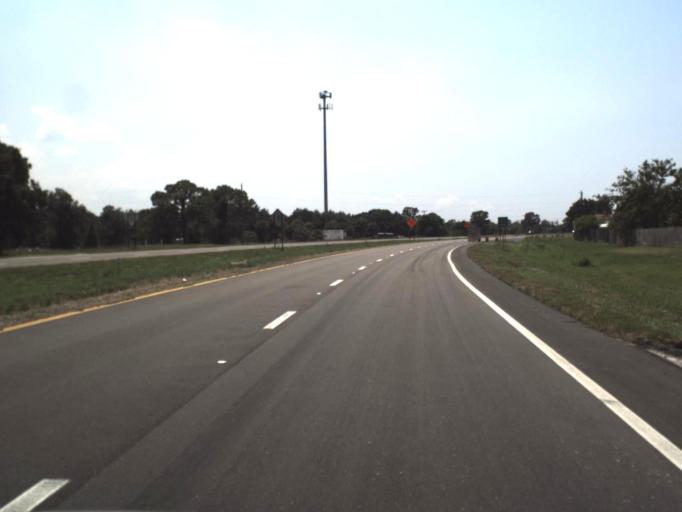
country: US
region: Florida
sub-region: Hillsborough County
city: Ruskin
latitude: 27.6764
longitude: -82.4788
